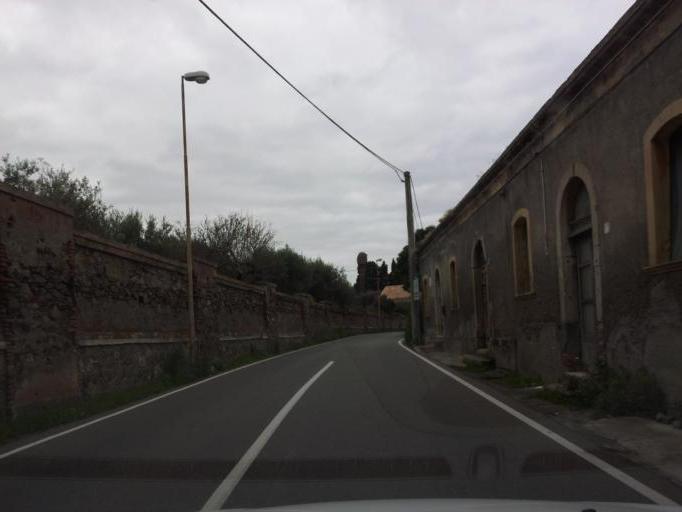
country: IT
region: Sicily
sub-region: Messina
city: Milazzo
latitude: 38.2406
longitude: 15.2473
